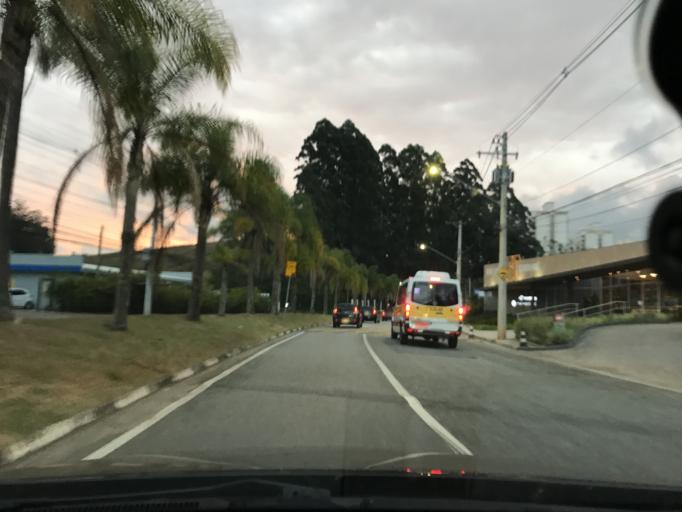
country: BR
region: Sao Paulo
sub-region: Carapicuiba
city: Carapicuiba
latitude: -23.4766
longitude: -46.8368
